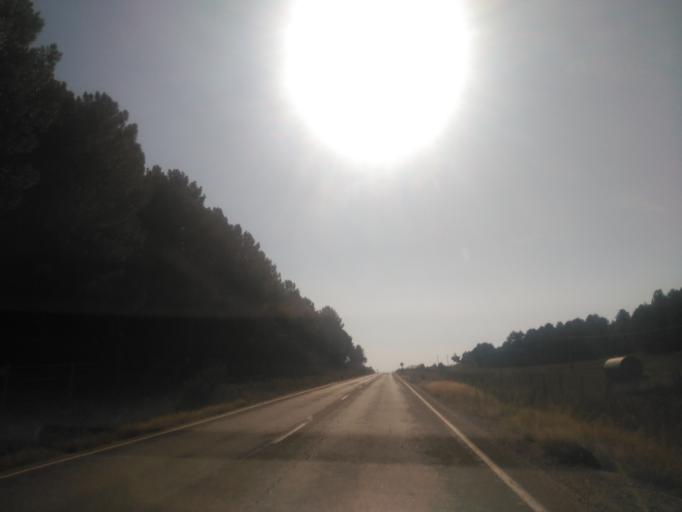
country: ES
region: Castille and Leon
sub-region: Provincia de Soria
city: Casarejos
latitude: 41.8066
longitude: -3.0524
